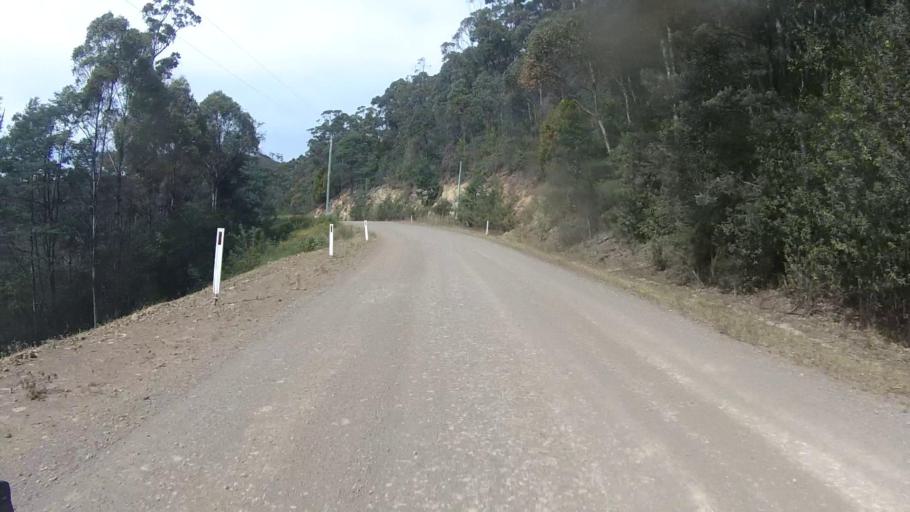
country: AU
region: Tasmania
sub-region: Sorell
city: Sorell
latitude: -42.7708
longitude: 147.8303
